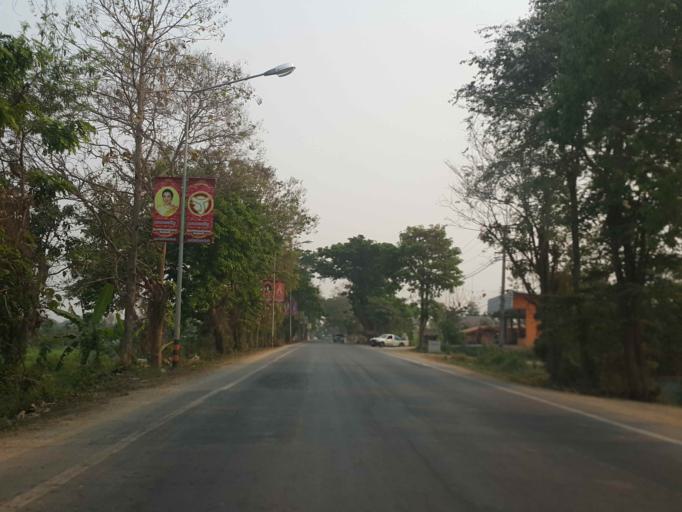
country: TH
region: Chiang Mai
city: Mae Taeng
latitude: 19.0069
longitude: 98.9718
